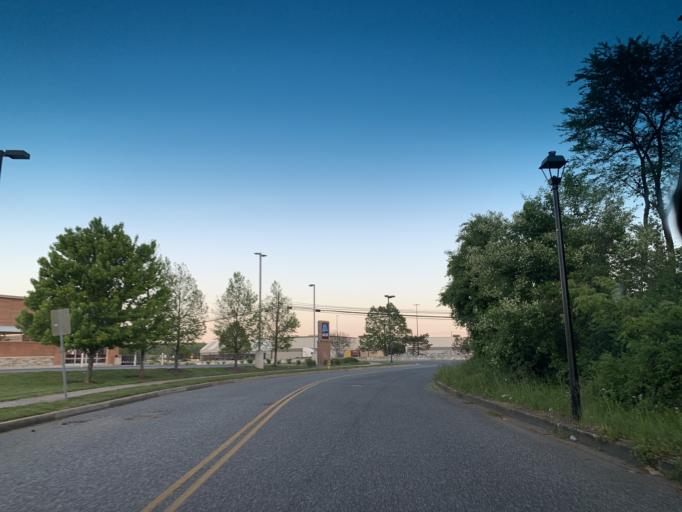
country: US
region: Maryland
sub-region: Harford County
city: Aberdeen
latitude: 39.4966
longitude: -76.1797
